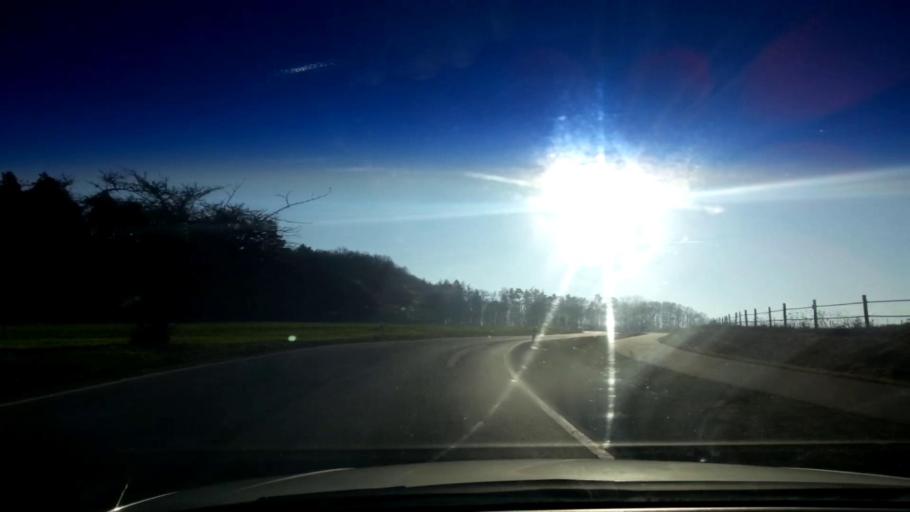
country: DE
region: Bavaria
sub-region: Upper Franconia
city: Litzendorf
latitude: 49.9362
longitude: 11.0101
